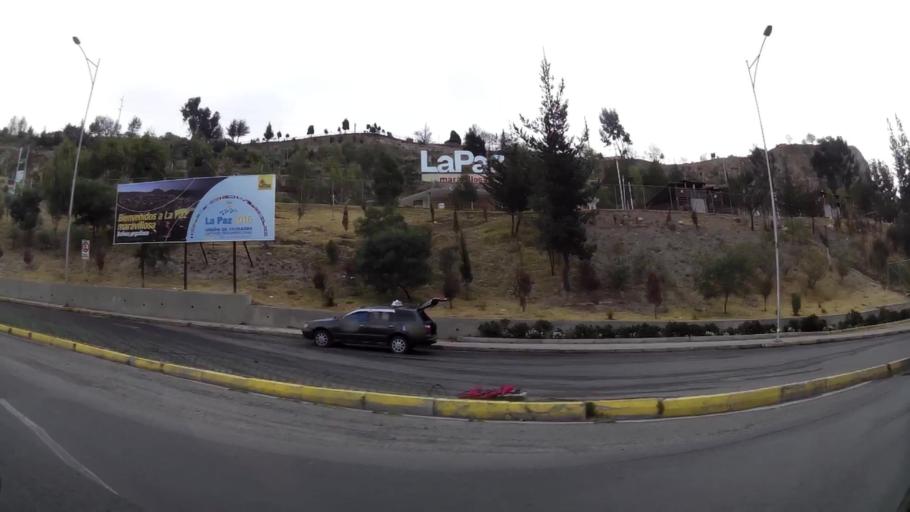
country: BO
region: La Paz
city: La Paz
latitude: -16.5041
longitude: -68.1259
